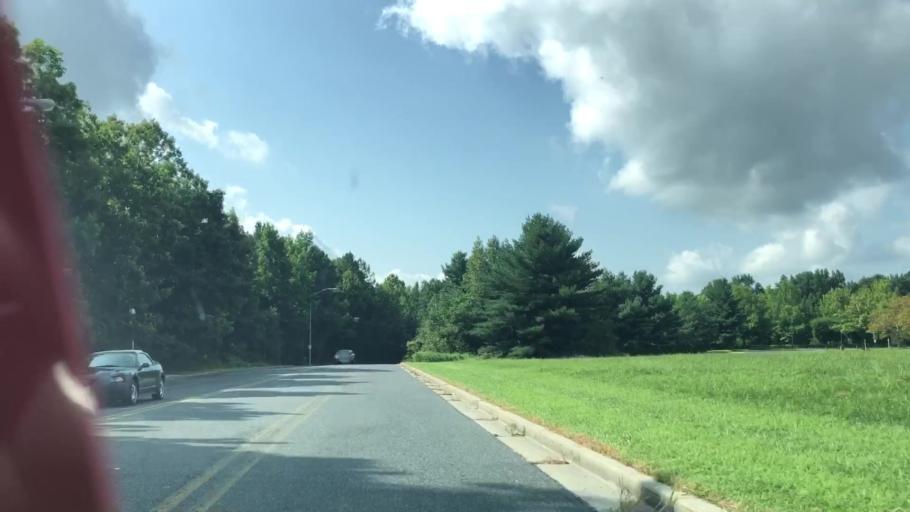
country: US
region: Maryland
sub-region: Wicomico County
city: Salisbury
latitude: 38.3975
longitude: -75.5628
